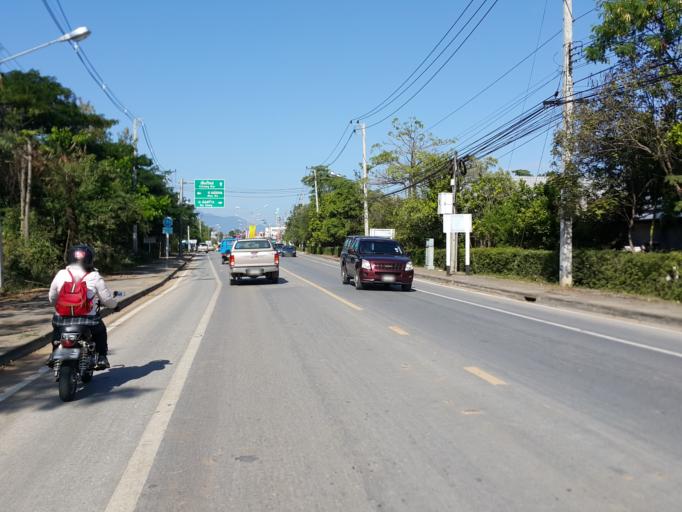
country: TH
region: Chiang Mai
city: San Kamphaeng
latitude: 18.7625
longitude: 99.0842
